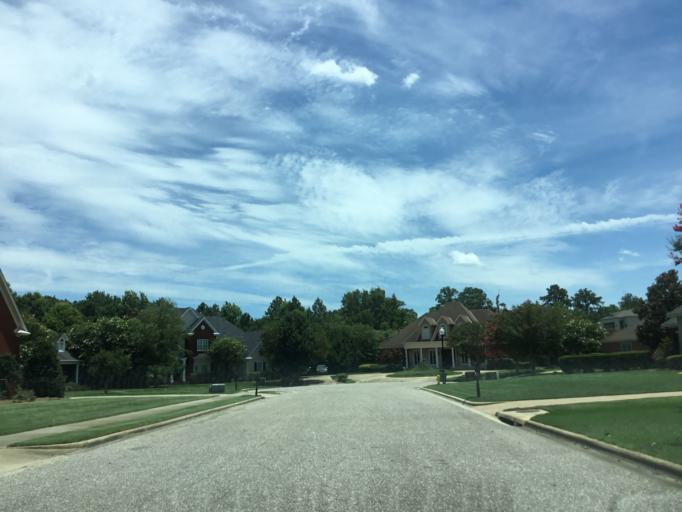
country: US
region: Alabama
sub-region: Montgomery County
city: Pike Road
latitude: 32.3751
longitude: -86.1285
